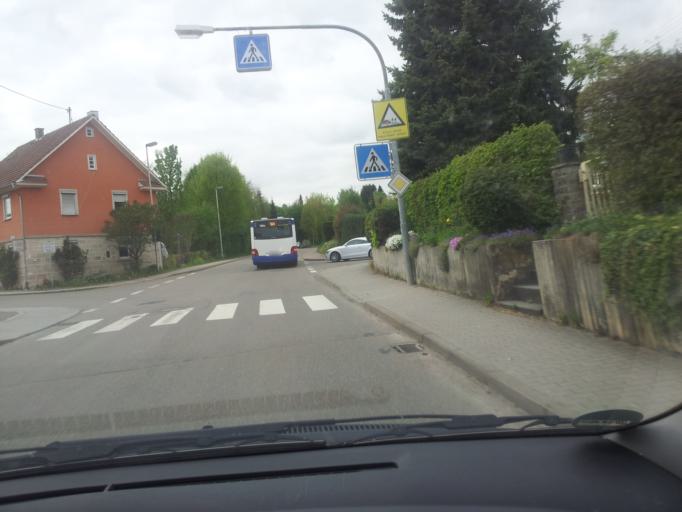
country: DE
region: Baden-Wuerttemberg
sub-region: Regierungsbezirk Stuttgart
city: Aspach
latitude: 48.9917
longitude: 9.3597
